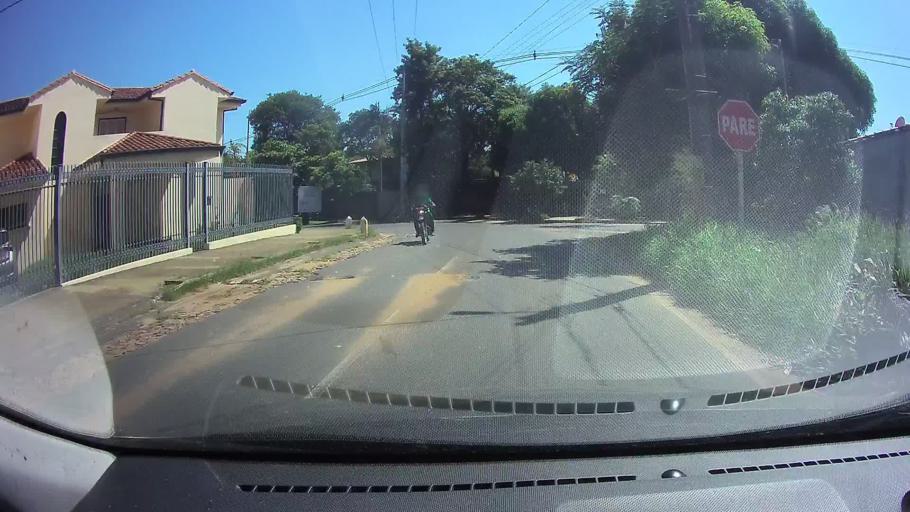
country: PY
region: Central
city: Fernando de la Mora
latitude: -25.3234
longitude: -57.5286
